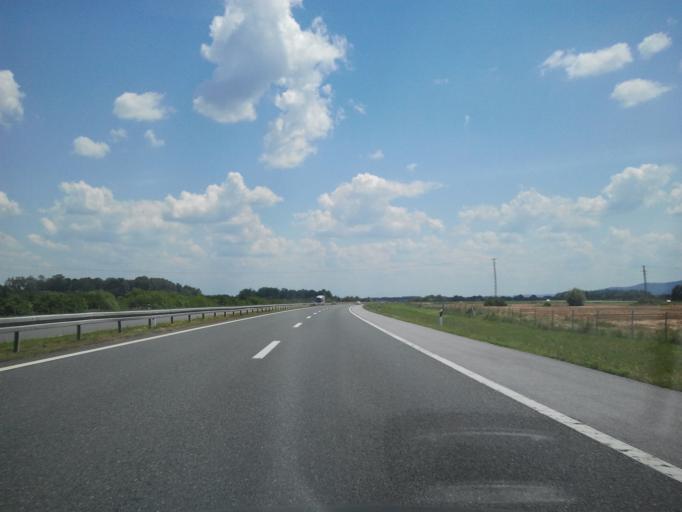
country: HR
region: Brodsko-Posavska
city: Batrina
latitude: 45.1861
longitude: 17.6375
